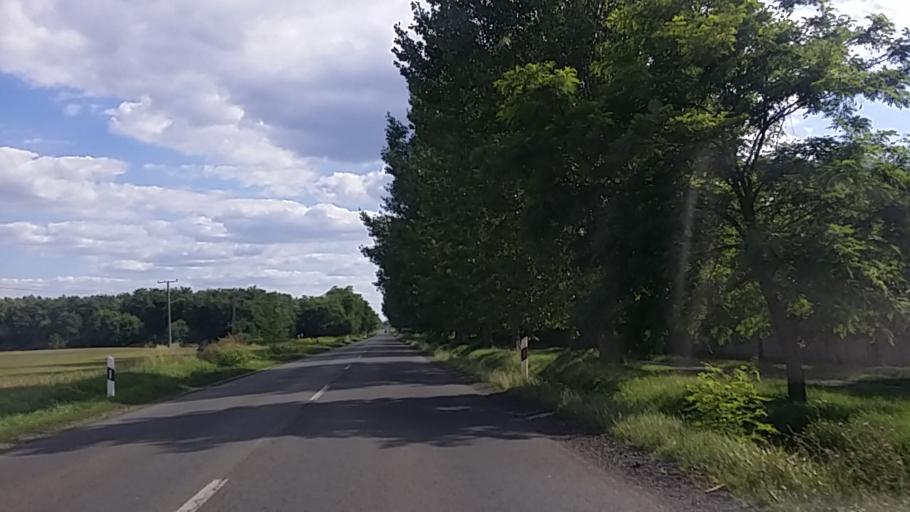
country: HU
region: Tolna
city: Dombovar
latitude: 46.3462
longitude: 18.1267
